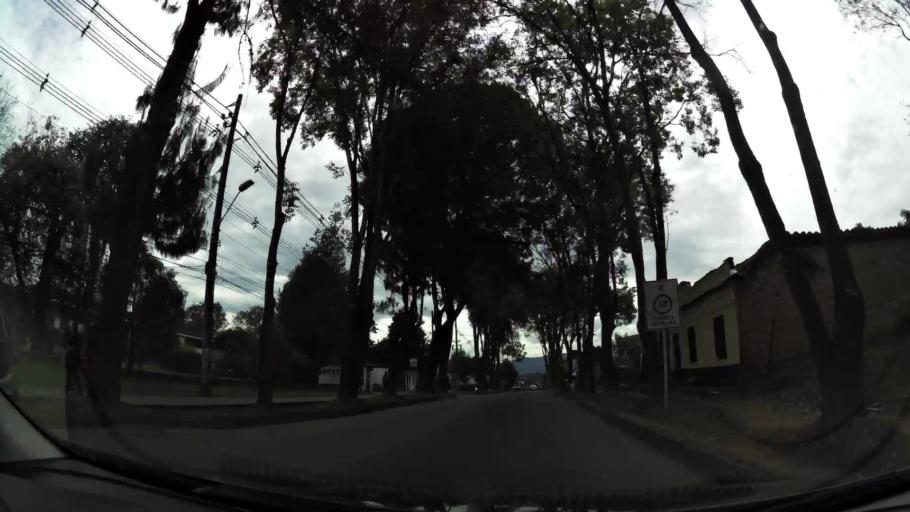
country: CO
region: Antioquia
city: Rionegro
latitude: 6.1514
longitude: -75.3840
